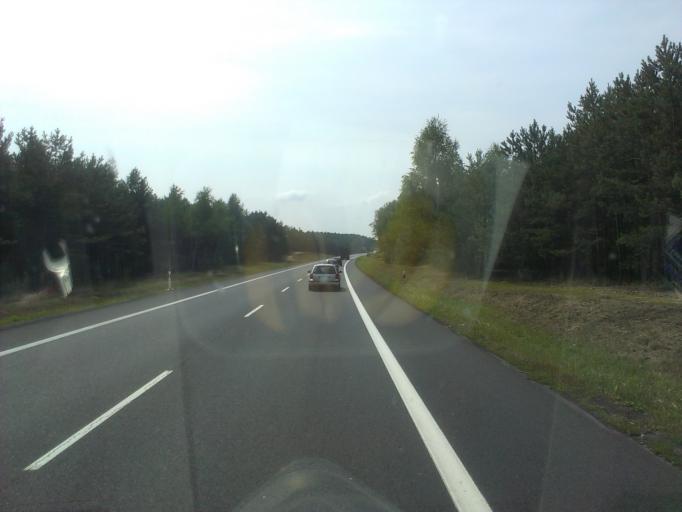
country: PL
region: Lubusz
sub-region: Zielona Gora
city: Zielona Gora
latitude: 51.9901
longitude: 15.5717
